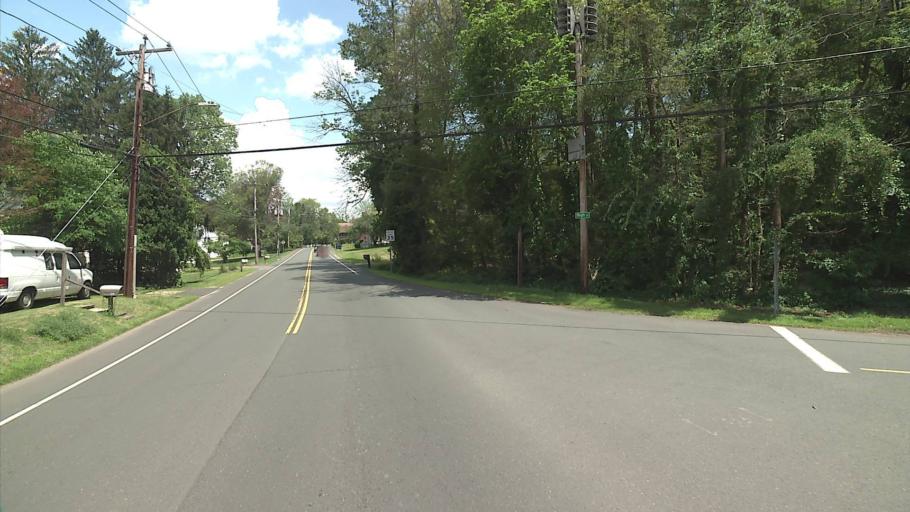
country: US
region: Connecticut
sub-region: Middlesex County
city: Higganum
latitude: 41.4973
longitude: -72.5545
